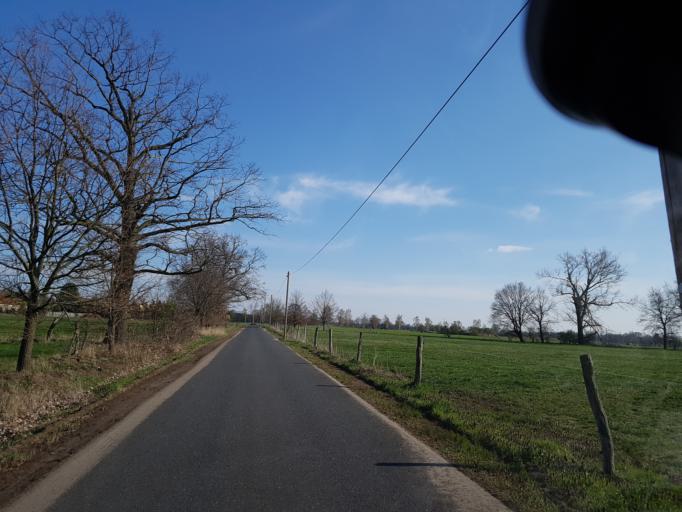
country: DE
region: Brandenburg
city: Schilda
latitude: 51.6292
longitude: 13.3116
